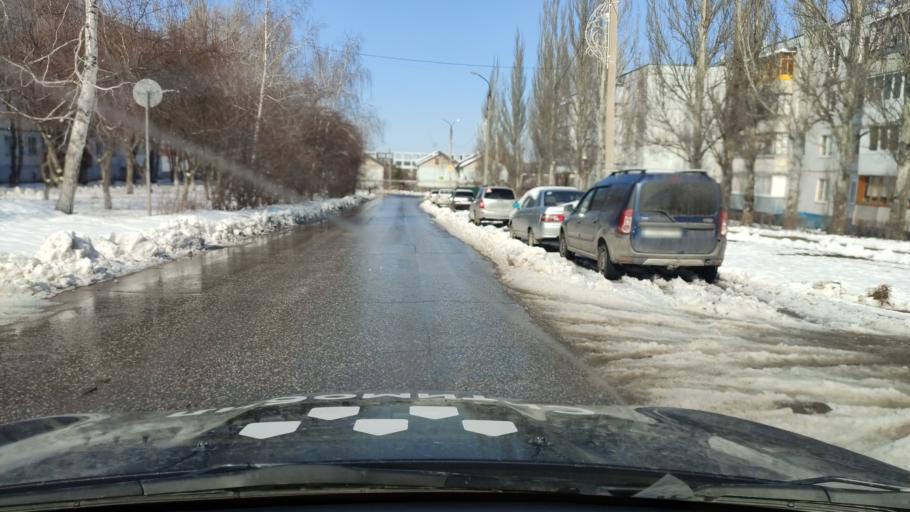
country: RU
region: Samara
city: Povolzhskiy
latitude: 53.5868
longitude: 49.7598
